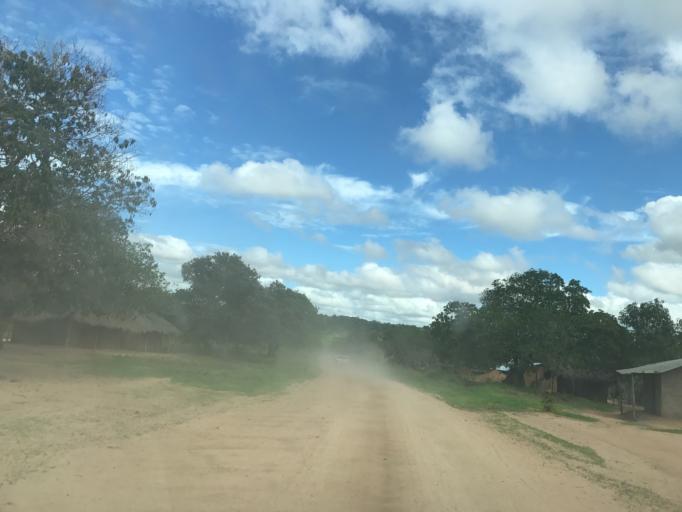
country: MZ
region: Nampula
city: Nacala
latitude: -14.4129
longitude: 40.5359
